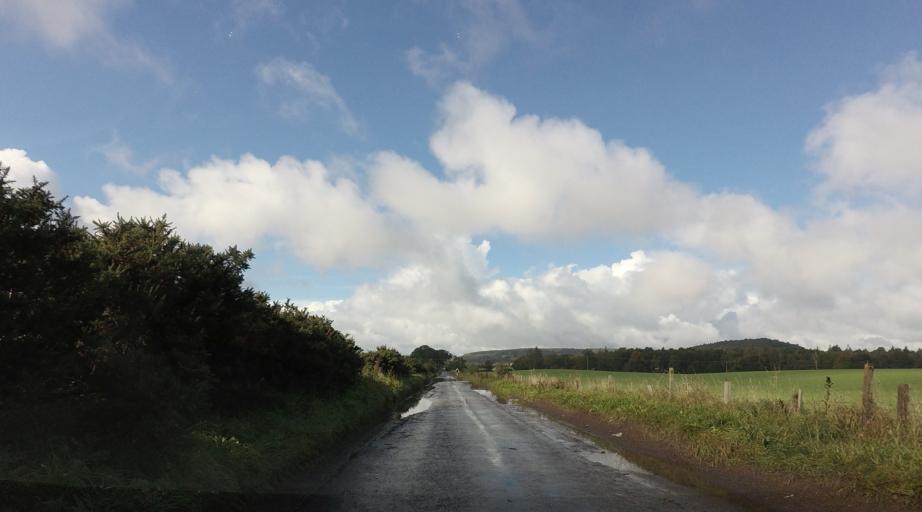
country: GB
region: Scotland
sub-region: Fife
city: Balmullo
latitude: 56.4066
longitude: -2.9280
